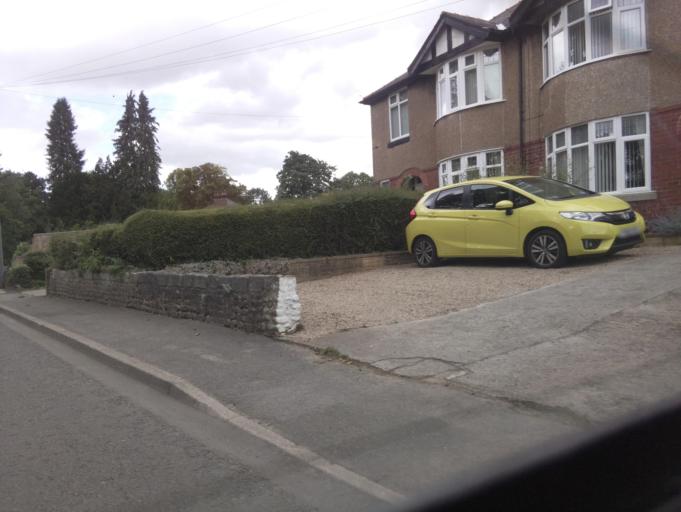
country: GB
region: England
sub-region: North Yorkshire
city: Ripon
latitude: 54.1432
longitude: -1.5255
